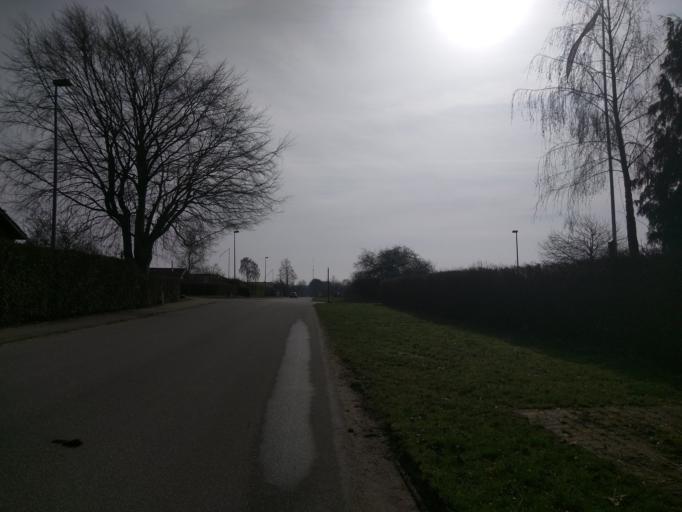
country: DK
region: South Denmark
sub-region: Fredericia Kommune
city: Snoghoj
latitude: 55.5460
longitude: 9.6984
